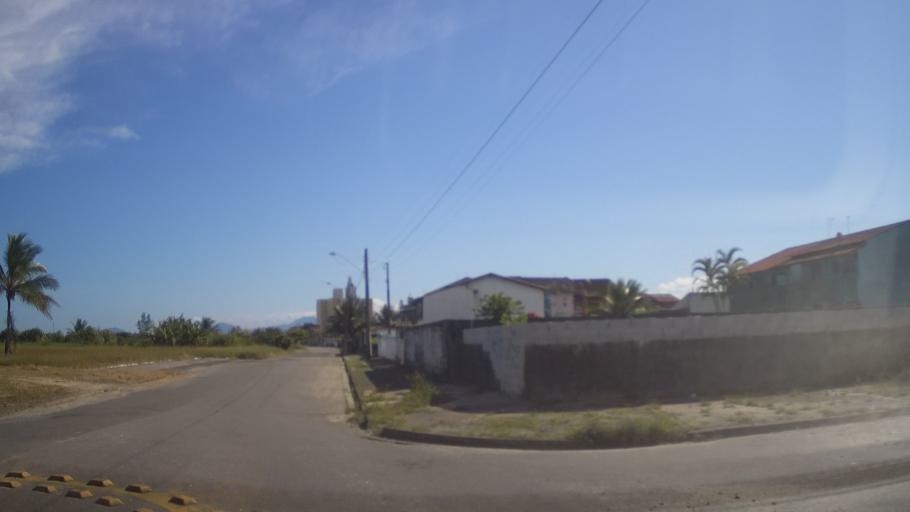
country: BR
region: Sao Paulo
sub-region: Itanhaem
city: Itanhaem
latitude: -24.2118
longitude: -46.8374
